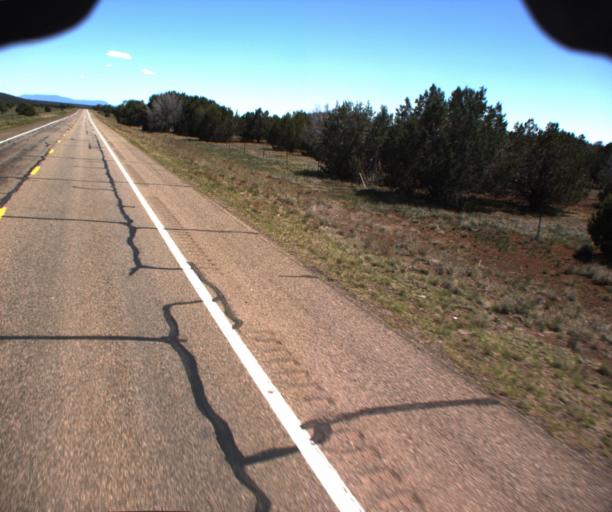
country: US
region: Arizona
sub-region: Yavapai County
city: Paulden
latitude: 35.1578
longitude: -112.4543
